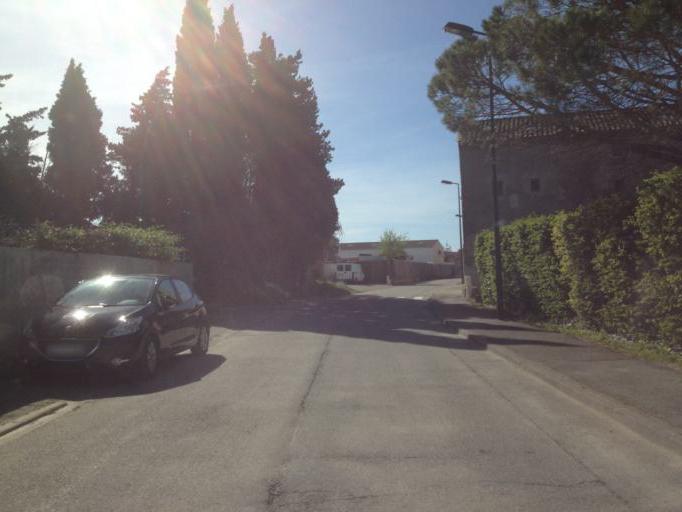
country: FR
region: Provence-Alpes-Cote d'Azur
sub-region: Departement du Vaucluse
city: Caderousse
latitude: 44.1061
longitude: 4.7553
